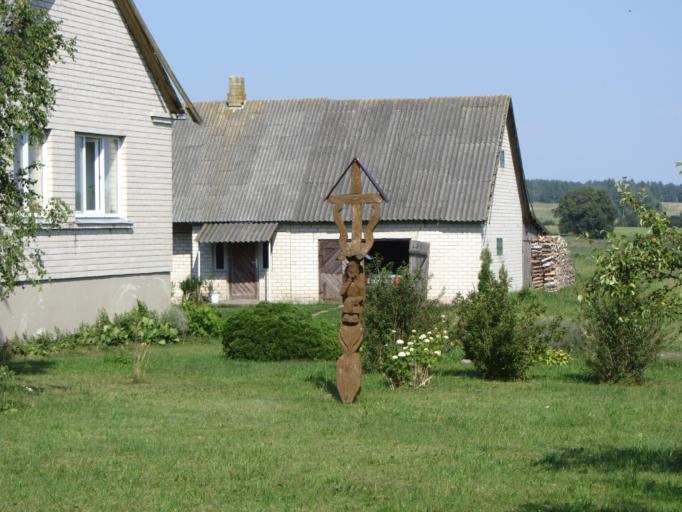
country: LT
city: Veisiejai
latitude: 54.1786
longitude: 23.7272
